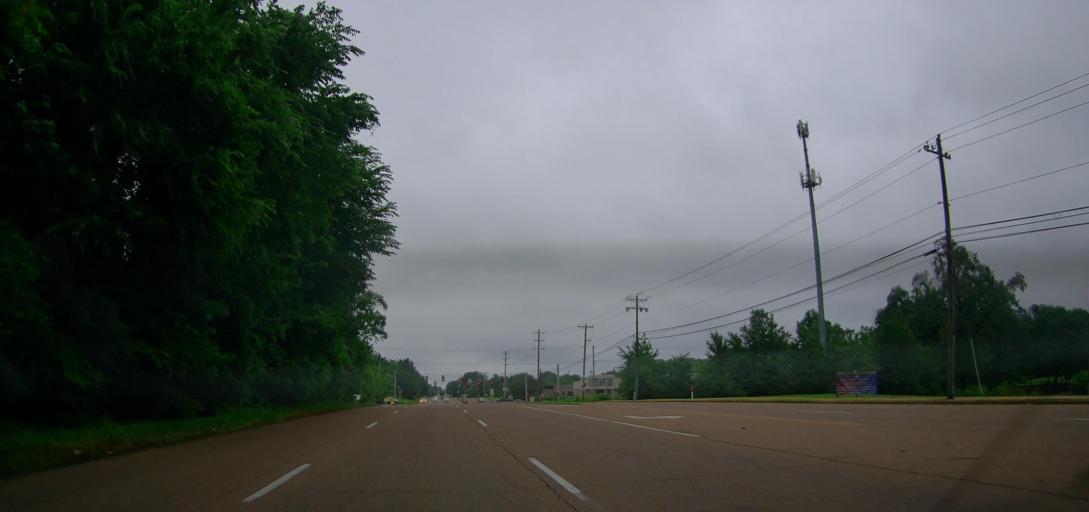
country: US
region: Mississippi
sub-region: De Soto County
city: Olive Branch
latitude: 35.0044
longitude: -89.8310
